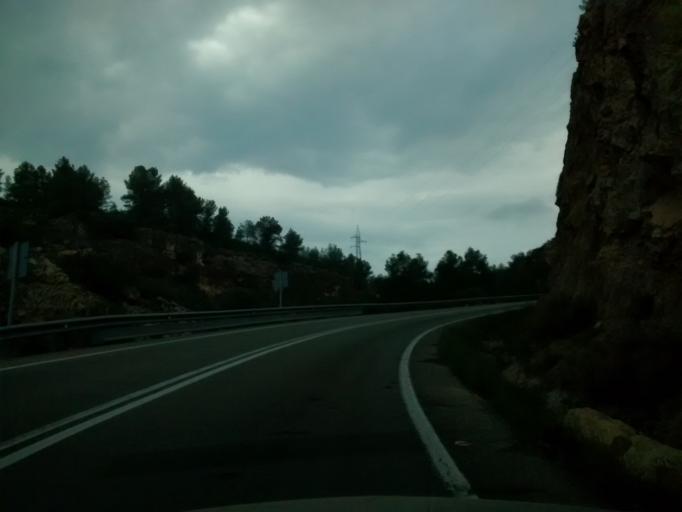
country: ES
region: Catalonia
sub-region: Provincia de Tarragona
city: Benifallet
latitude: 40.9886
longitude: 0.5131
